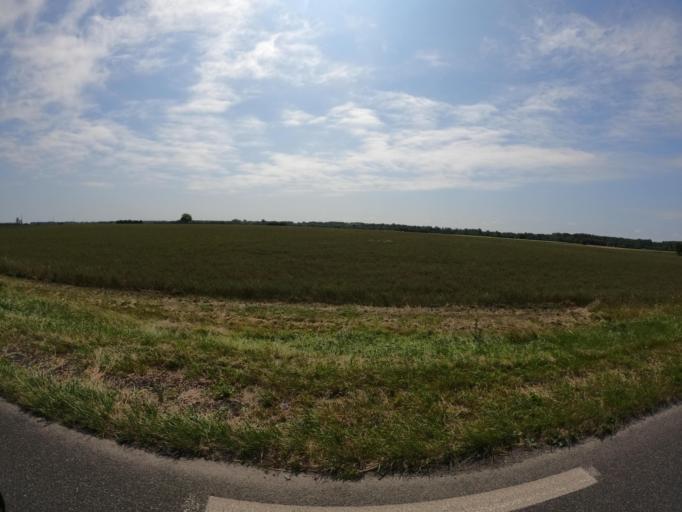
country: FR
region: Poitou-Charentes
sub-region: Departement des Deux-Sevres
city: Frontenay-Rohan-Rohan
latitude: 46.2450
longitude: -0.5684
